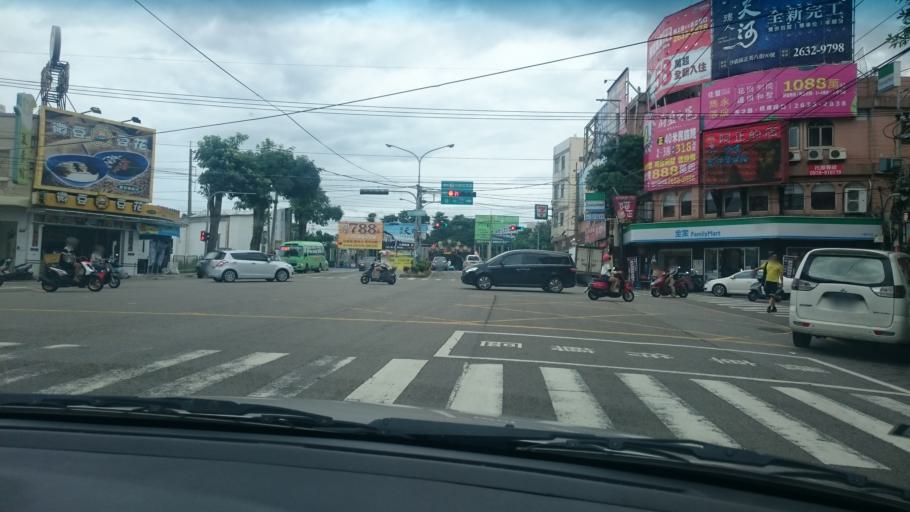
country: TW
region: Taiwan
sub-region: Taichung City
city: Taichung
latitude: 24.2267
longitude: 120.5750
